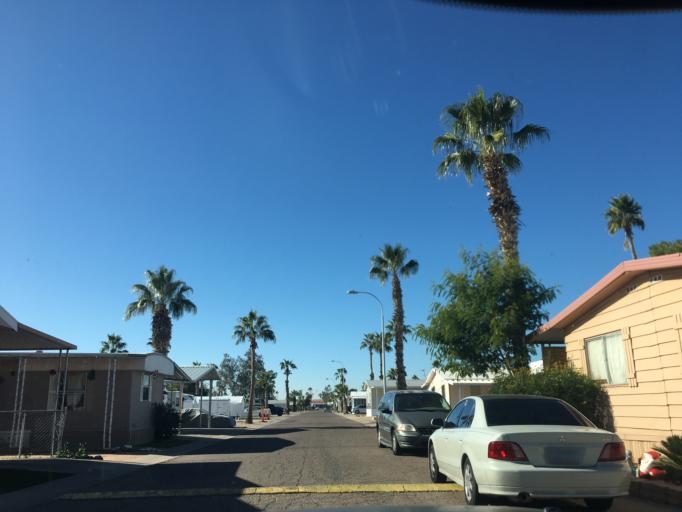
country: US
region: Arizona
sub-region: Maricopa County
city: Mesa
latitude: 33.4490
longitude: -111.8448
